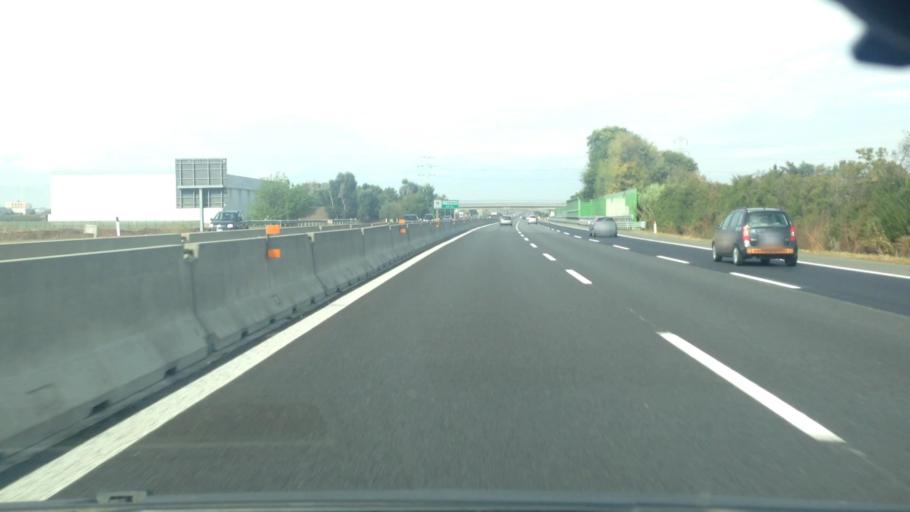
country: IT
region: Piedmont
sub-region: Provincia di Torino
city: Tagliaferro
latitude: 44.9785
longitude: 7.6508
